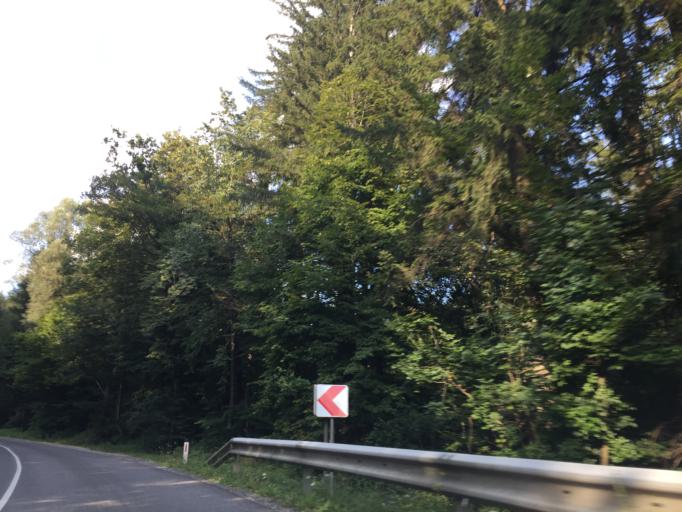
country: SI
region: Naklo
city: Naklo
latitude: 46.2954
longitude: 14.2652
